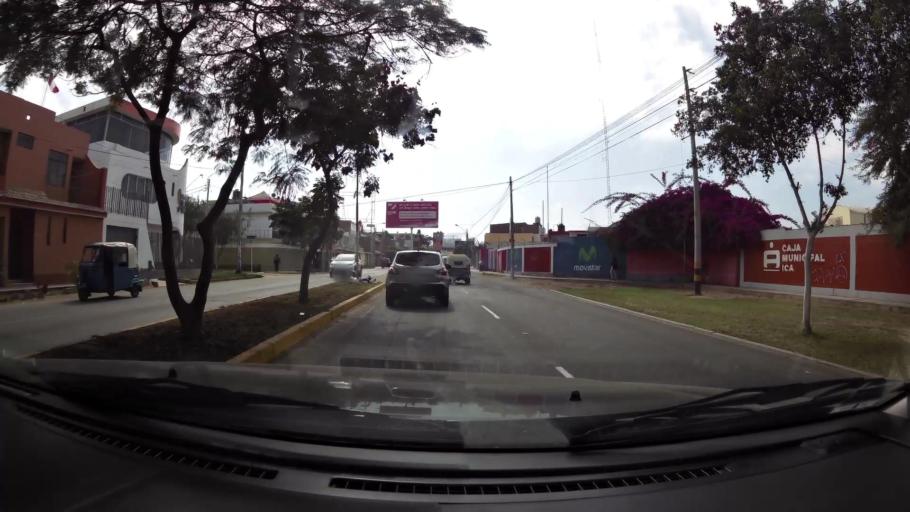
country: PE
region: Ica
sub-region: Provincia de Ica
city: Ica
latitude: -14.0736
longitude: -75.7315
